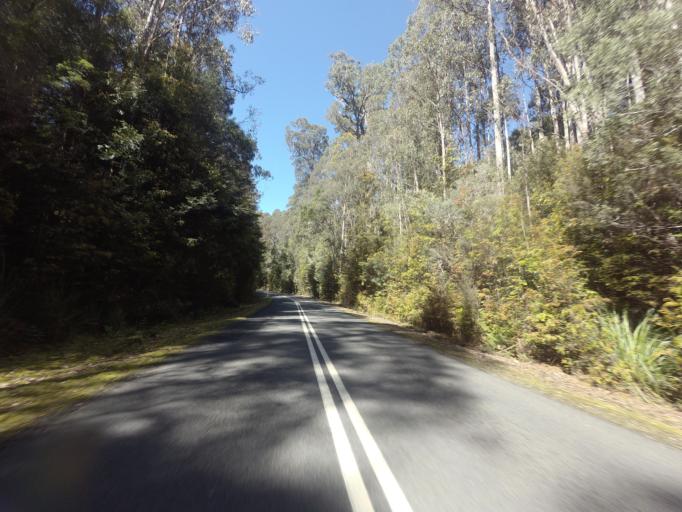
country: AU
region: Tasmania
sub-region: Huon Valley
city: Geeveston
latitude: -42.8205
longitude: 146.3012
